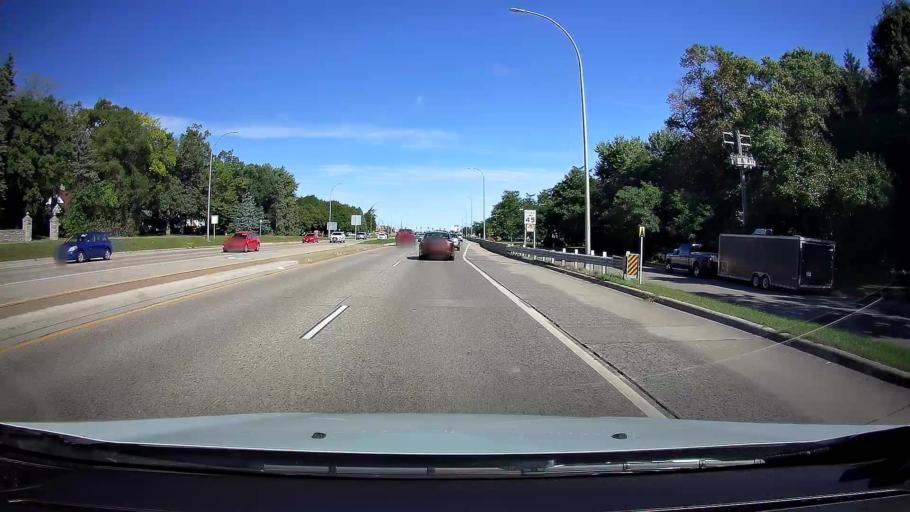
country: US
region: Minnesota
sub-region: Ramsey County
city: Falcon Heights
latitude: 44.9995
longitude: -93.1665
